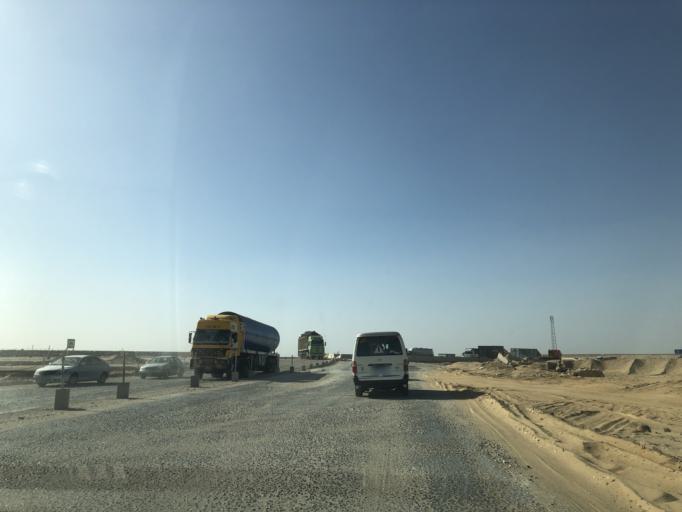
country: EG
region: Muhafazat al Minufiyah
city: Ashmun
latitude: 30.0624
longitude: 30.8467
